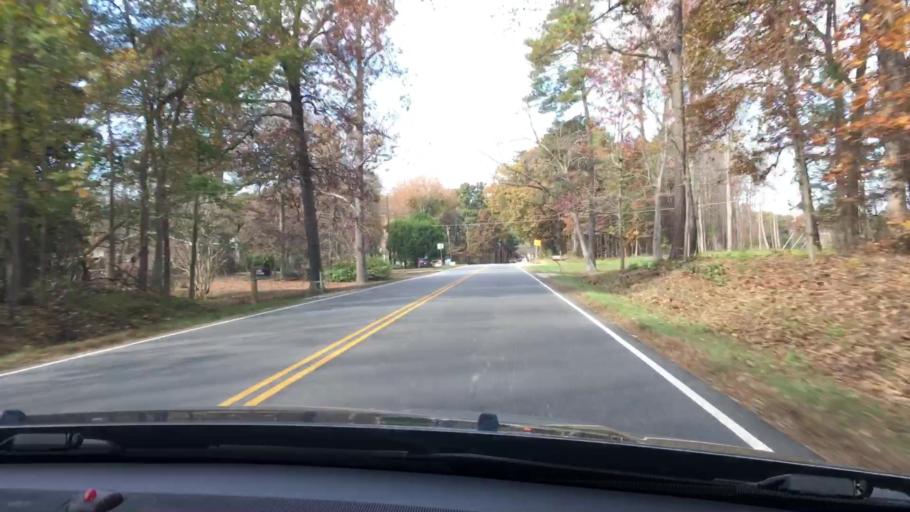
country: US
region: Virginia
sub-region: King William County
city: West Point
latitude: 37.4342
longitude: -76.8340
